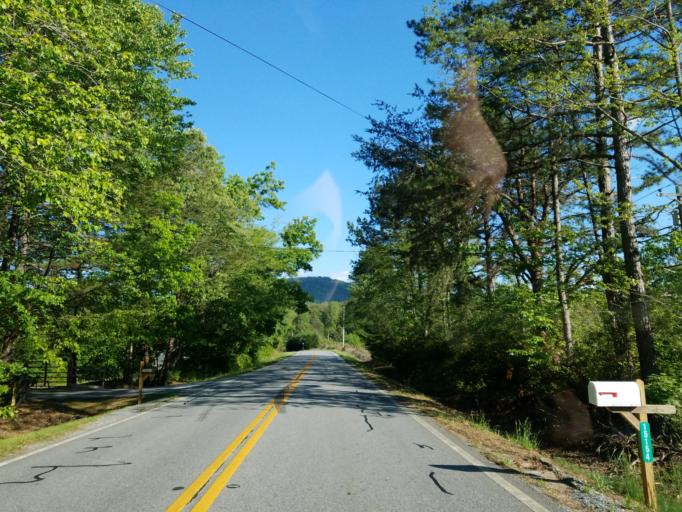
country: US
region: Georgia
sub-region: Fannin County
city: Blue Ridge
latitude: 34.8486
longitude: -84.2180
